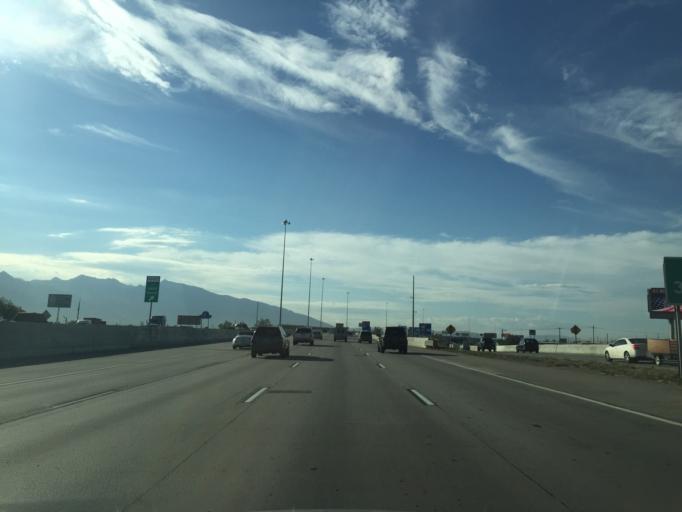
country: US
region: Utah
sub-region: Salt Lake County
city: Centerfield
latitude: 40.7031
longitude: -111.9036
